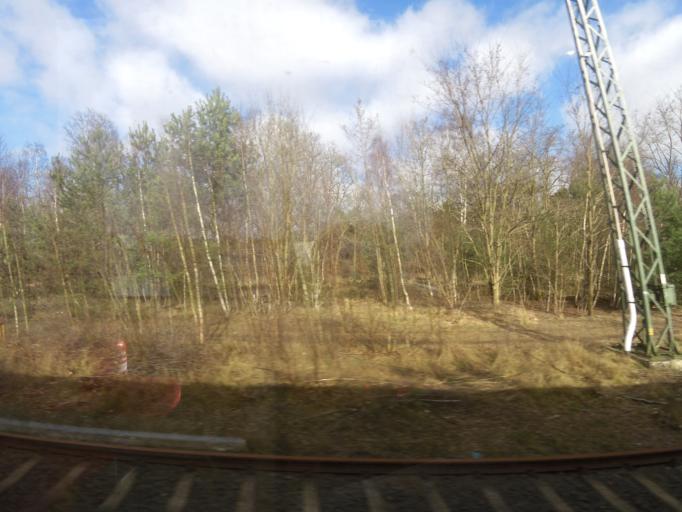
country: DE
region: Lower Saxony
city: Buchholz in der Nordheide
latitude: 53.3233
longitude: 9.8625
